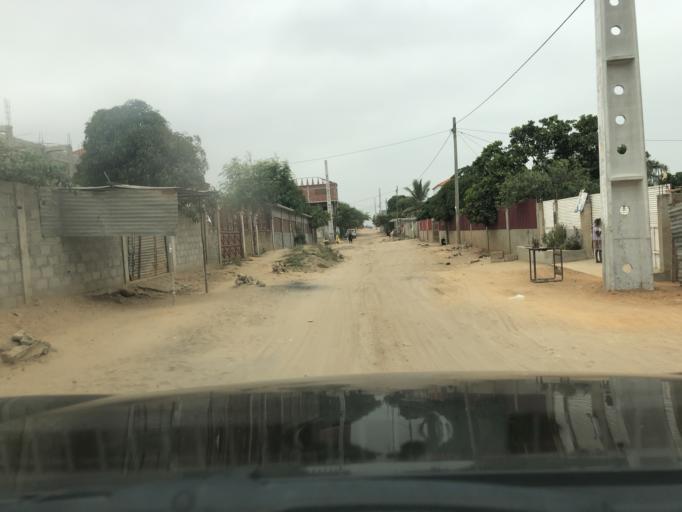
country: AO
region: Luanda
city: Luanda
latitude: -8.9373
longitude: 13.2262
